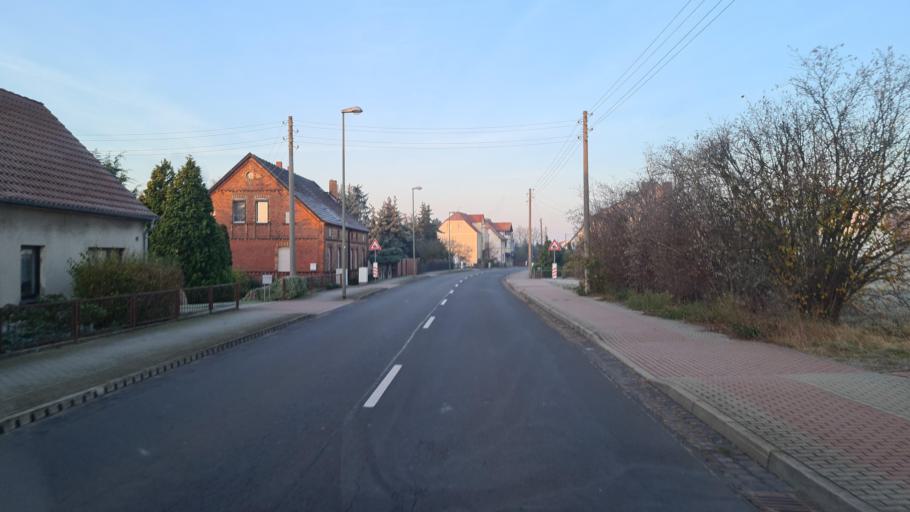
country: DE
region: Saxony-Anhalt
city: Holzdorf
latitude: 51.7788
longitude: 13.1187
